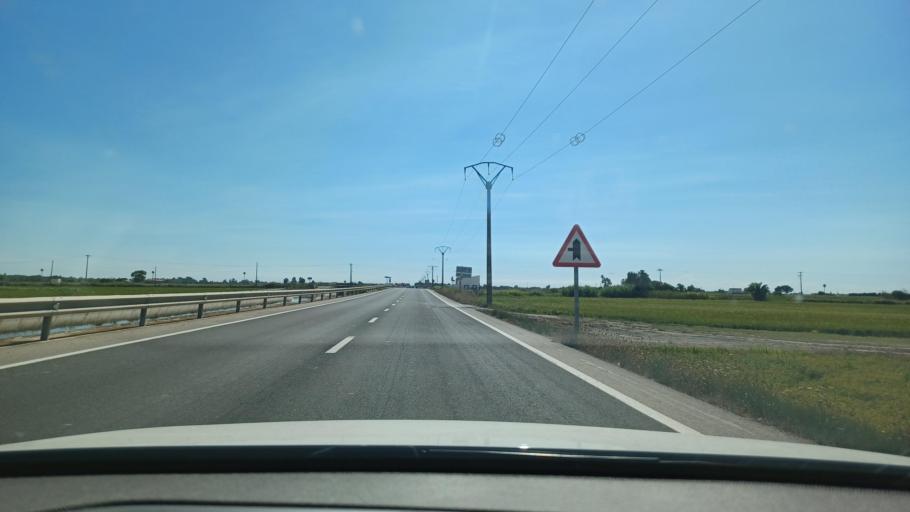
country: ES
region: Catalonia
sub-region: Provincia de Tarragona
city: Deltebre
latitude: 40.7099
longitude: 0.6821
